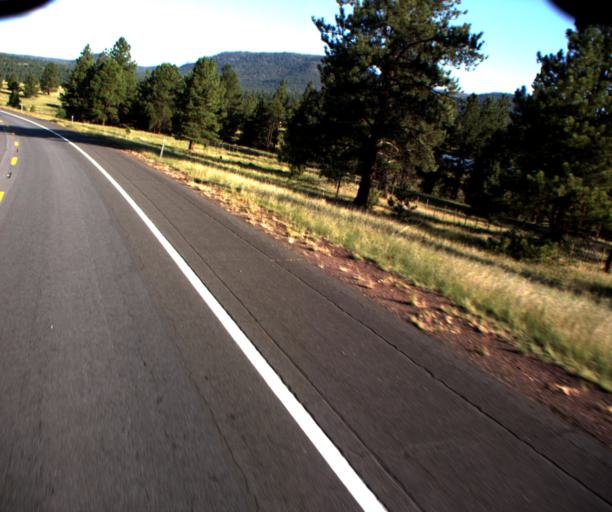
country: US
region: New Mexico
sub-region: Catron County
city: Reserve
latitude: 33.8257
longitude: -109.0817
